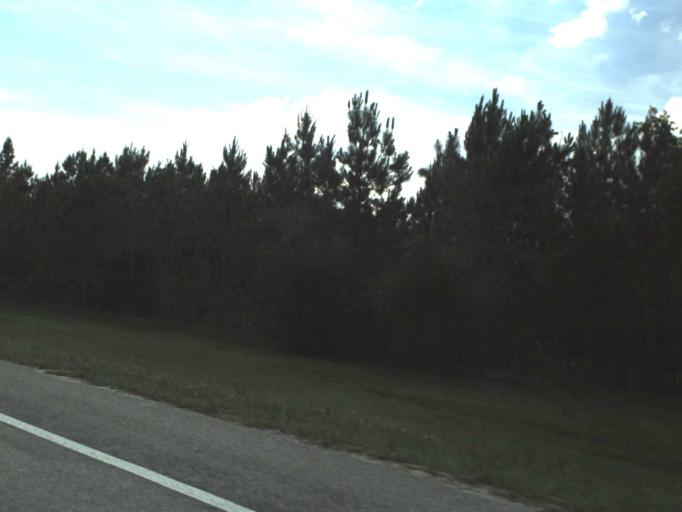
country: US
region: Florida
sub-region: Volusia County
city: Samsula-Spruce Creek
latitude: 29.0253
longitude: -81.1288
